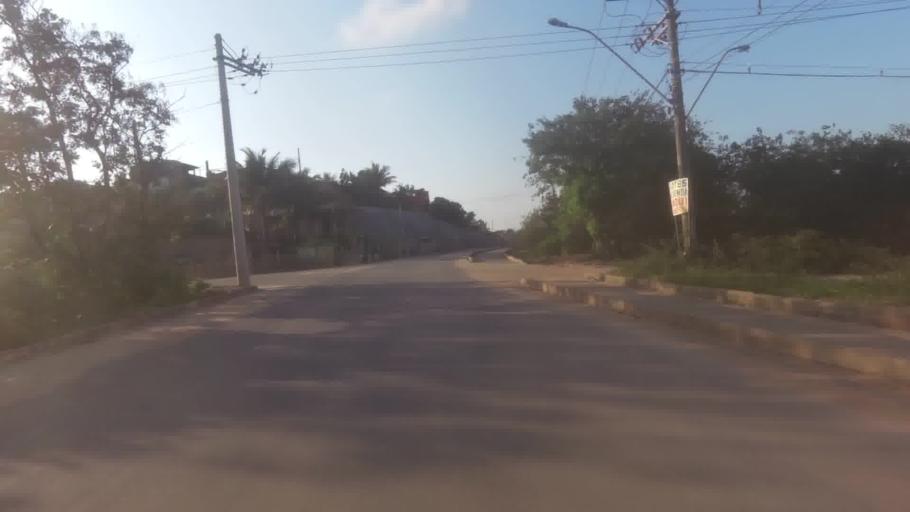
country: BR
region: Espirito Santo
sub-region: Itapemirim
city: Itapemirim
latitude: -21.0177
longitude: -40.8279
